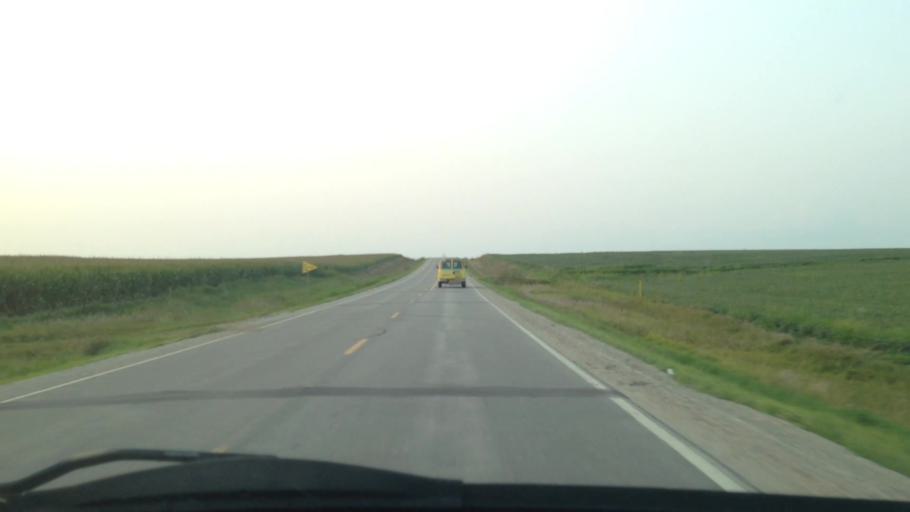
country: US
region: Iowa
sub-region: Benton County
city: Atkins
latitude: 42.0276
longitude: -91.8740
